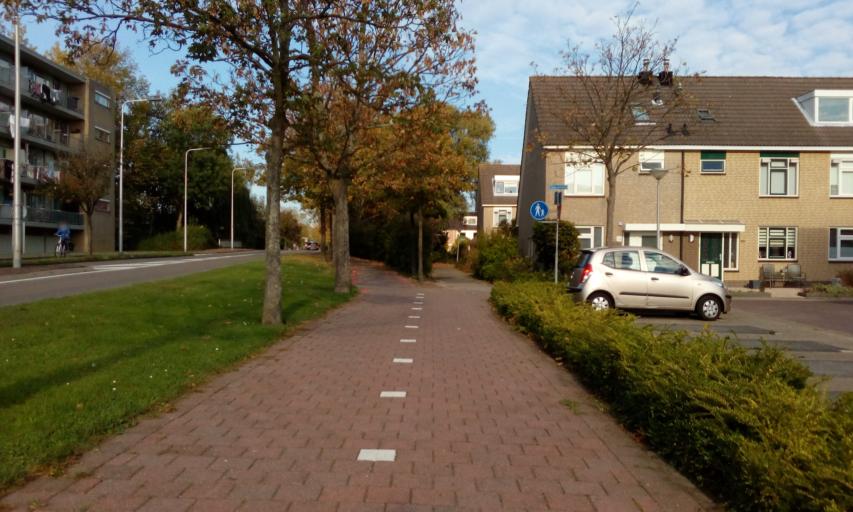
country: NL
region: South Holland
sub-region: Gemeente Westland
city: Naaldwijk
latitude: 51.9930
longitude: 4.2171
